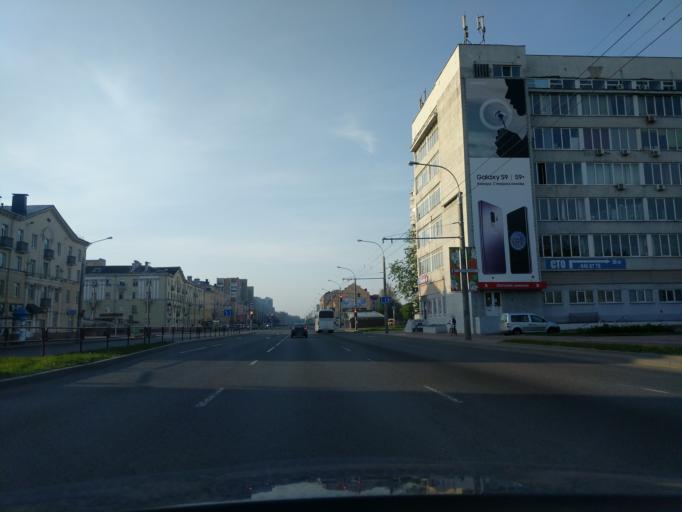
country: BY
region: Minsk
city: Minsk
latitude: 53.8629
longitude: 27.5716
